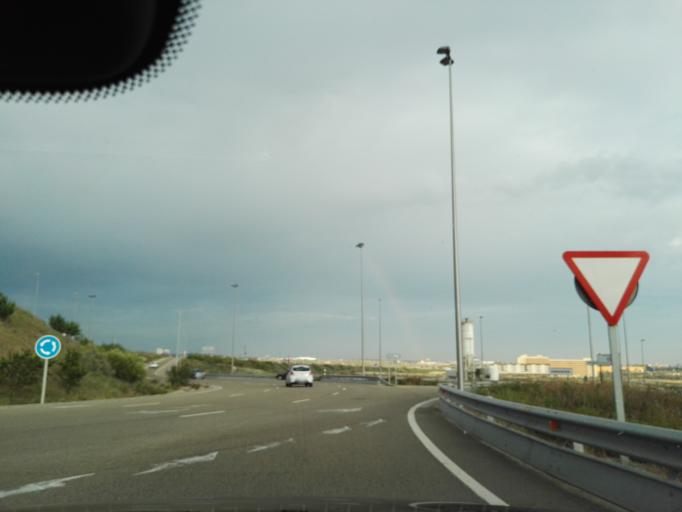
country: ES
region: Aragon
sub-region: Provincia de Zaragoza
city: Montecanal
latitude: 41.6192
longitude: -0.9602
